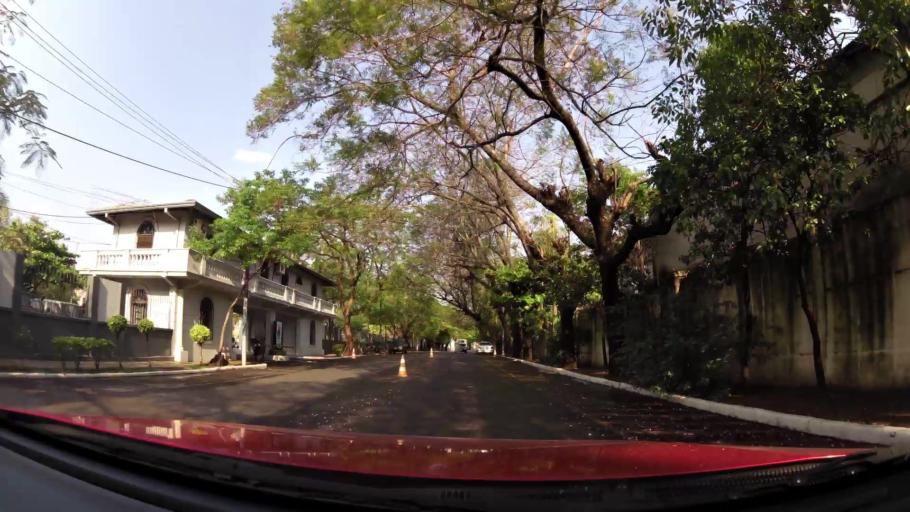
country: PY
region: Asuncion
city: Asuncion
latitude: -25.2765
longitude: -57.6424
